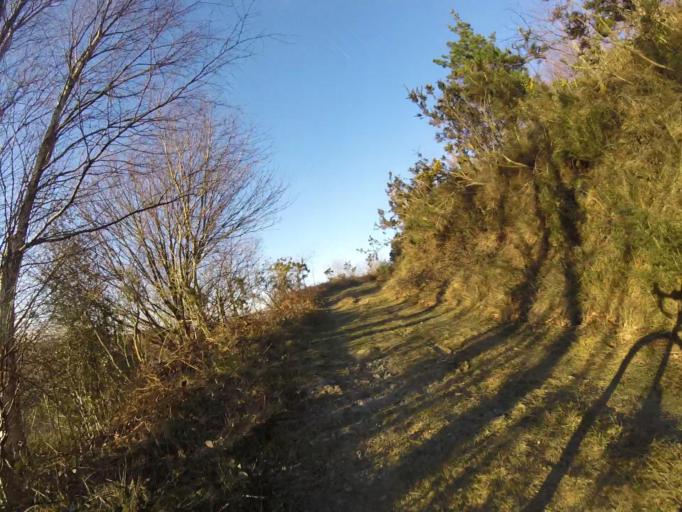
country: ES
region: Navarre
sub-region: Provincia de Navarra
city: Arano
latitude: 43.2565
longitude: -1.8411
